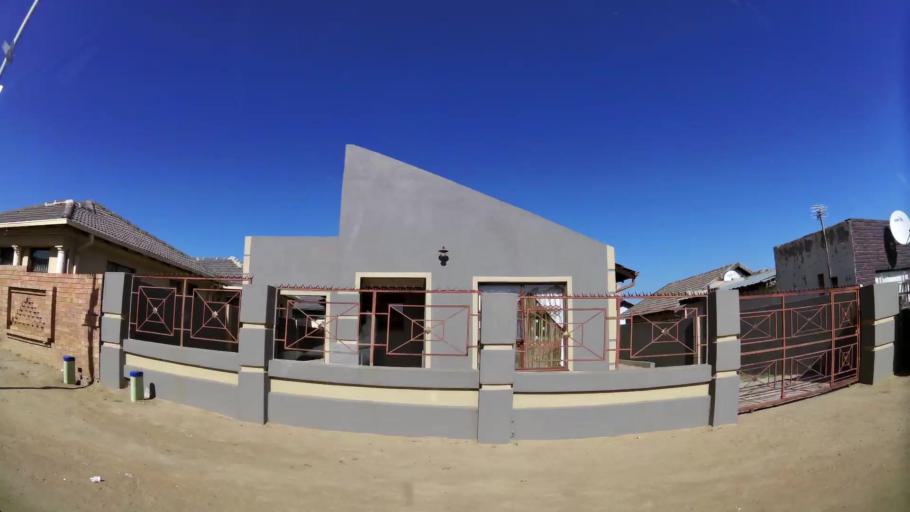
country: ZA
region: Gauteng
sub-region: Ekurhuleni Metropolitan Municipality
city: Tembisa
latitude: -26.0360
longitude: 28.1952
